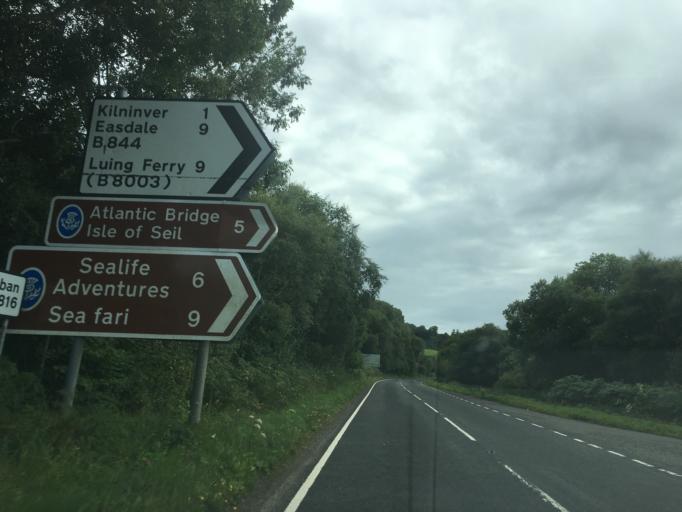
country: GB
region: Scotland
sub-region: Argyll and Bute
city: Oban
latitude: 56.3466
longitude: -5.5056
